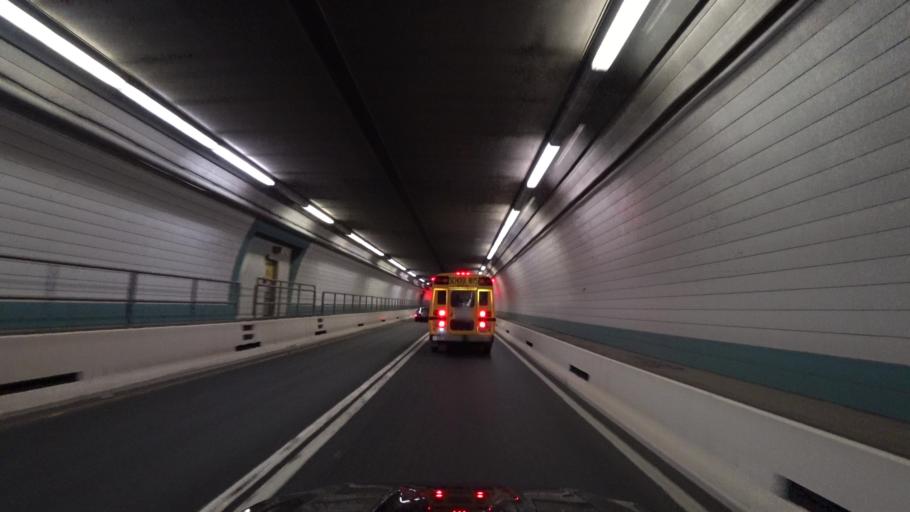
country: US
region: Massachusetts
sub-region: Suffolk County
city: Chelsea
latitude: 42.3609
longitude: -71.0281
